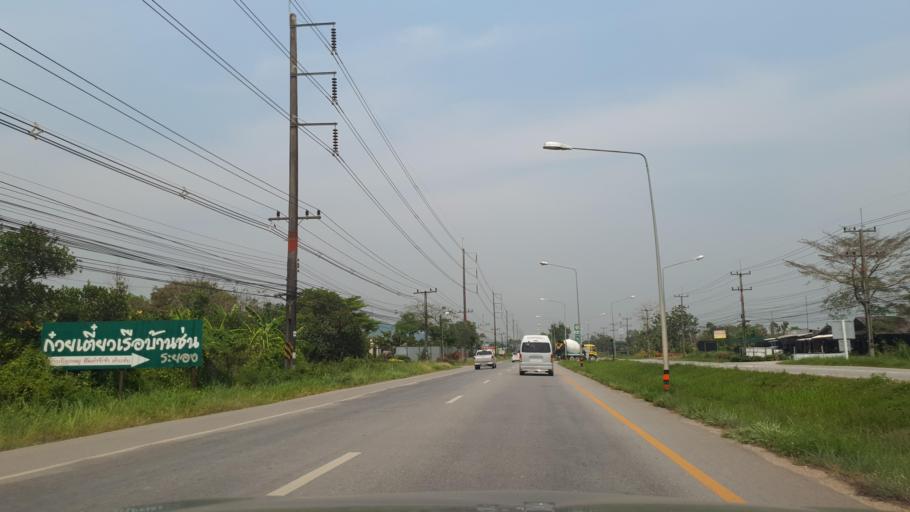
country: TH
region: Rayong
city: Rayong
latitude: 12.6398
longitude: 101.3842
